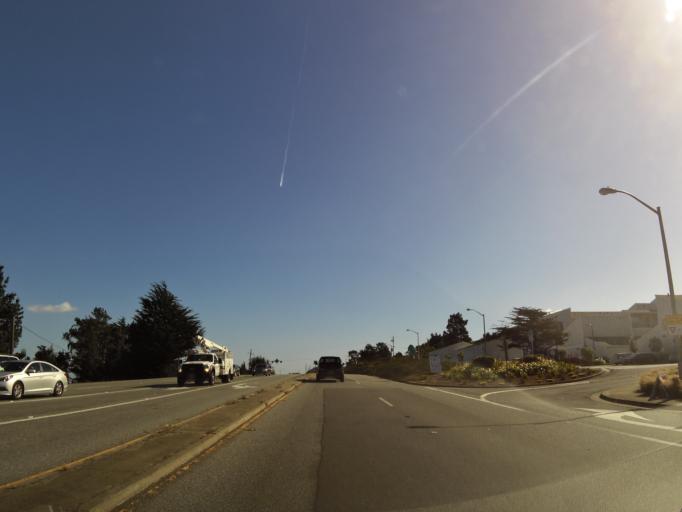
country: US
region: California
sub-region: San Mateo County
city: Pacifica
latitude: 37.6386
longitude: -122.4639
